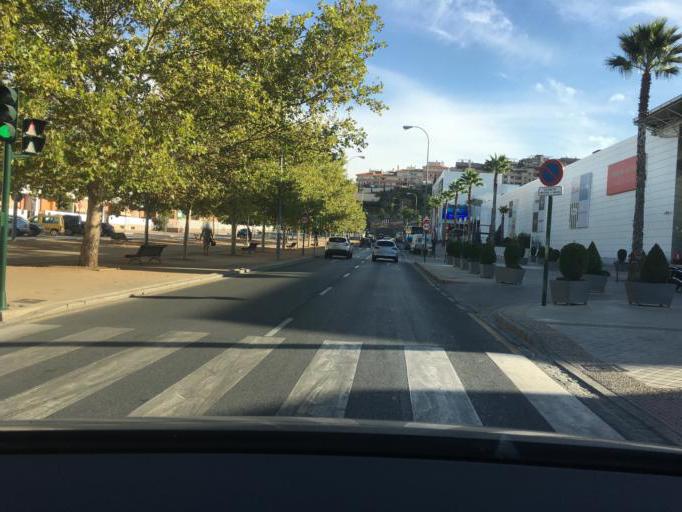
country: ES
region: Andalusia
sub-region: Provincia de Granada
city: Huetor Vega
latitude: 37.1563
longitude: -3.5852
